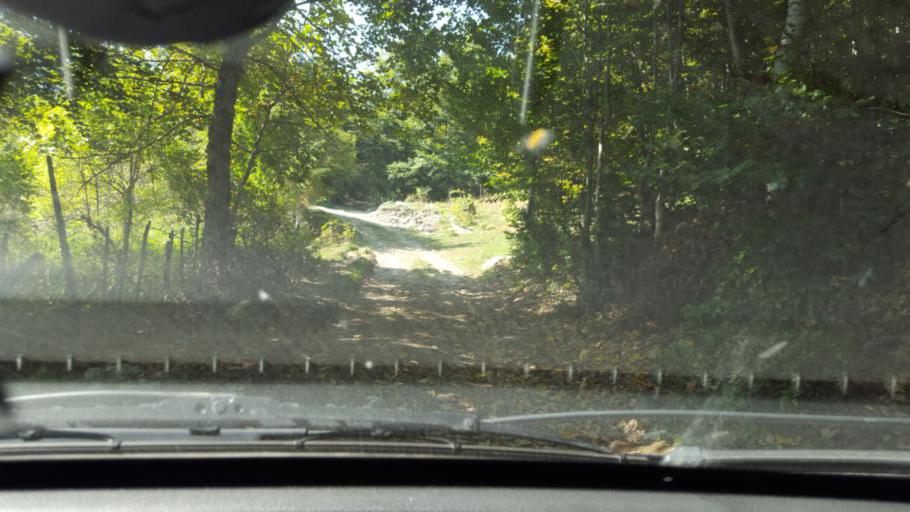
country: ME
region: Andrijevica
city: Andrijevica
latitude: 42.5870
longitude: 19.6352
